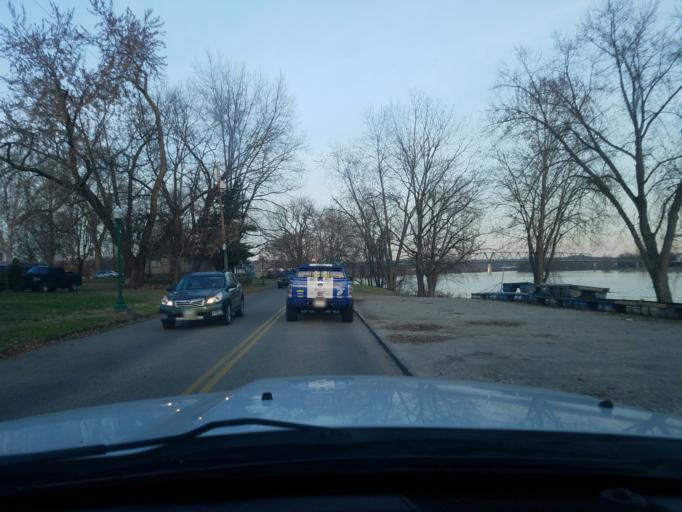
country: US
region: Ohio
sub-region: Washington County
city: Marietta
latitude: 39.4073
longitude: -81.4607
